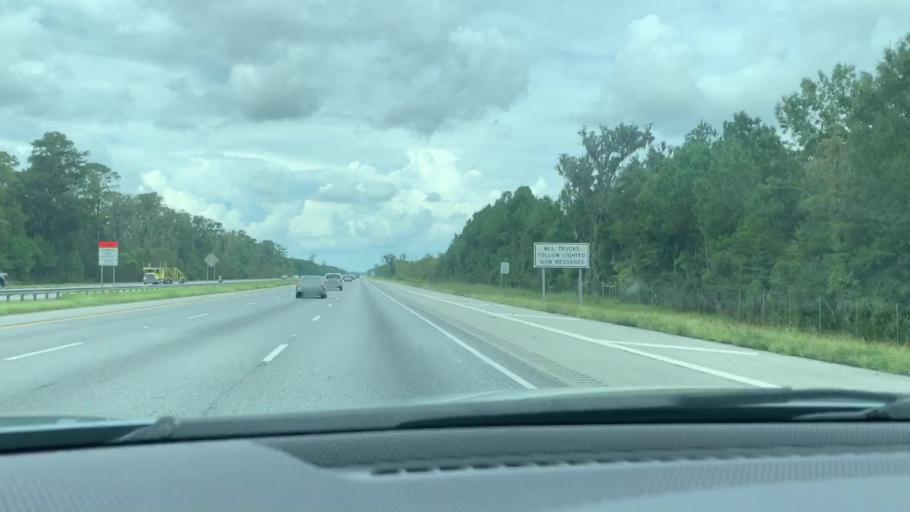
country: US
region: Georgia
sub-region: McIntosh County
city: Darien
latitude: 31.4423
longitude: -81.4444
